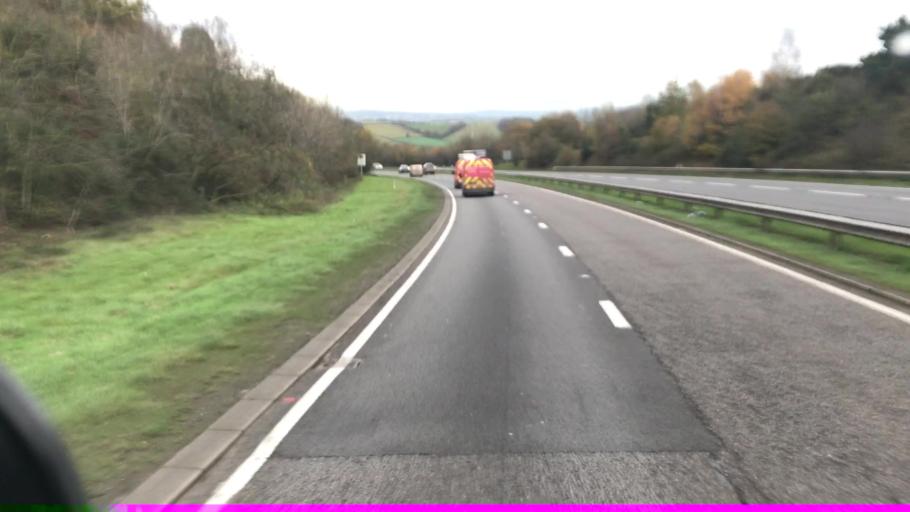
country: GB
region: England
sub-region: Devon
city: Exminster
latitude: 50.6485
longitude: -3.5428
